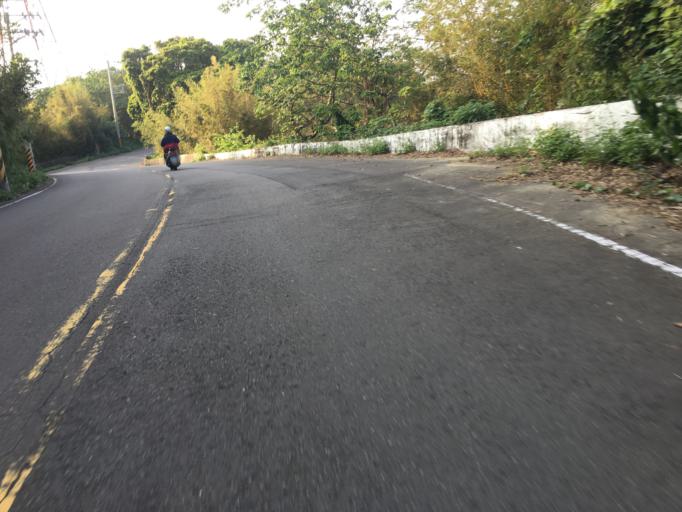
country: TW
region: Taiwan
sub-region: Hsinchu
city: Hsinchu
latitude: 24.7383
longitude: 121.0316
